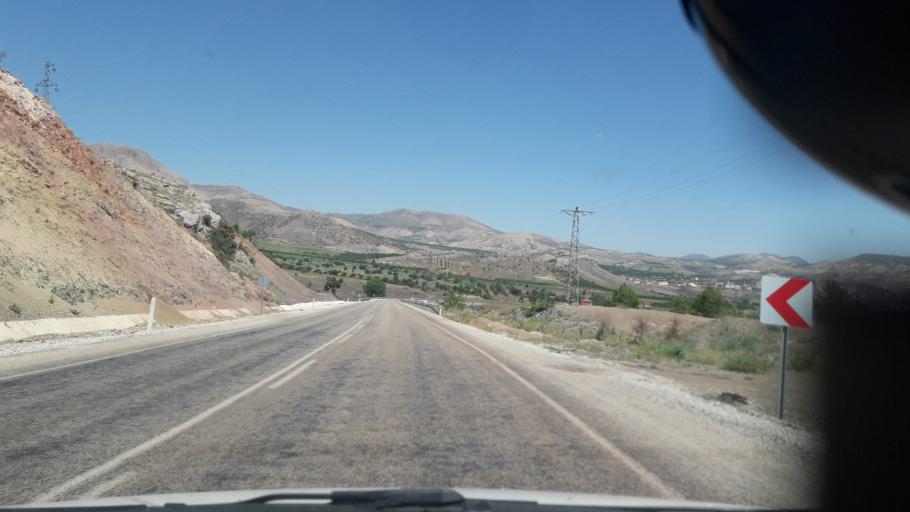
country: TR
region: Malatya
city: Hekimhan
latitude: 38.8209
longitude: 37.8817
